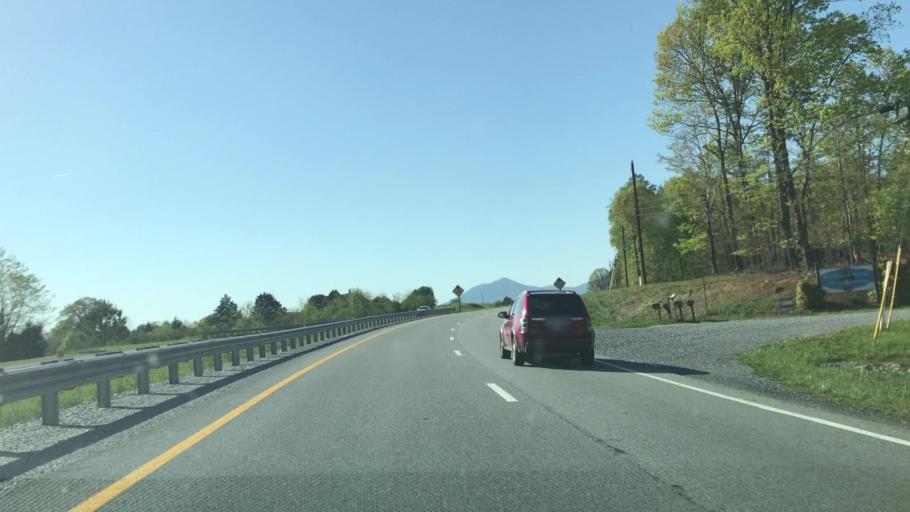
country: US
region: Virginia
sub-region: City of Bedford
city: Bedford
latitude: 37.3149
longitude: -79.4799
